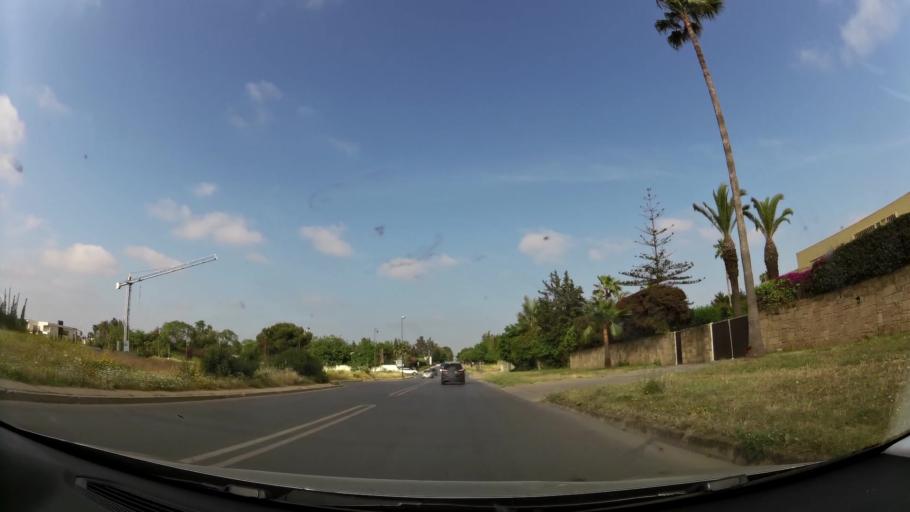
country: MA
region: Rabat-Sale-Zemmour-Zaer
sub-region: Rabat
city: Rabat
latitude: 33.9603
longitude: -6.8384
